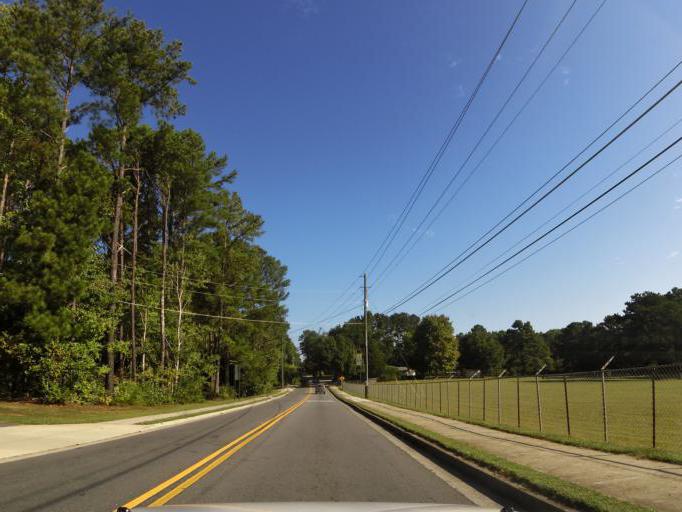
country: US
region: Georgia
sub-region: Cobb County
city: Acworth
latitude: 34.0134
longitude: -84.6757
